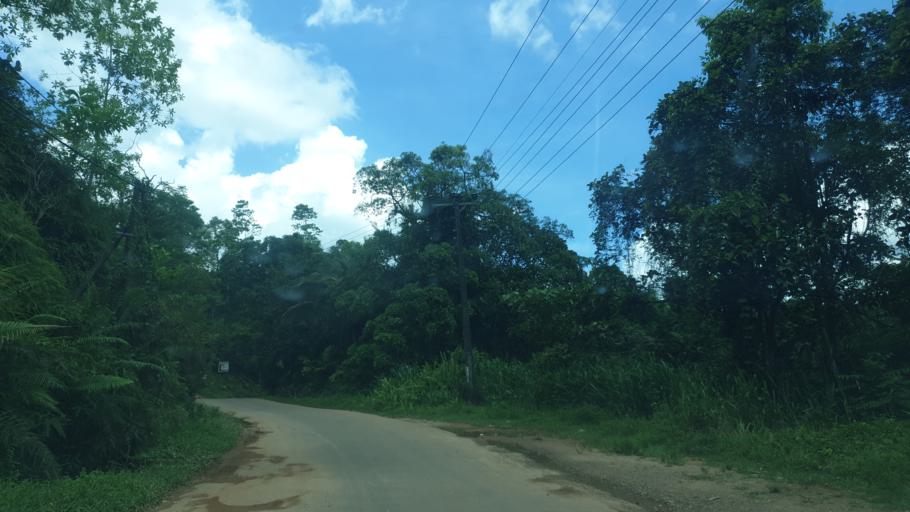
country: LK
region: Sabaragamuwa
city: Ratnapura
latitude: 6.4815
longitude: 80.4122
